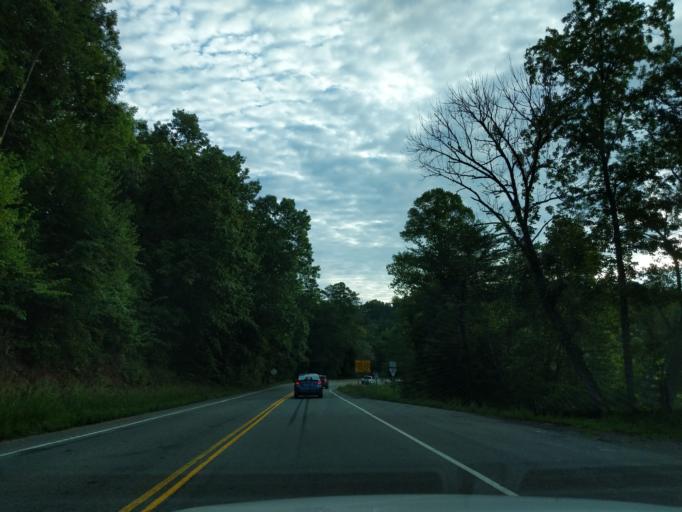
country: US
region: Tennessee
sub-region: Polk County
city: Benton
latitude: 35.1123
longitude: -84.5807
